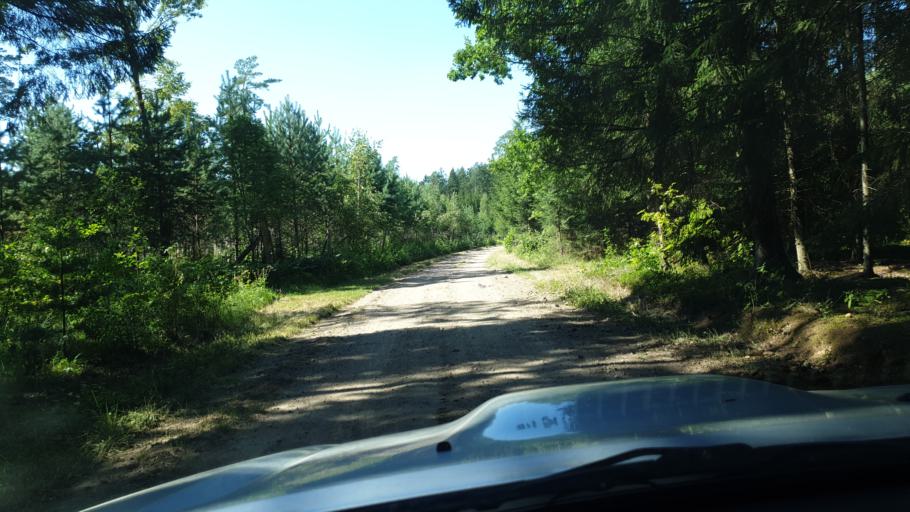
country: LT
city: Sirvintos
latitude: 54.9071
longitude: 24.9434
